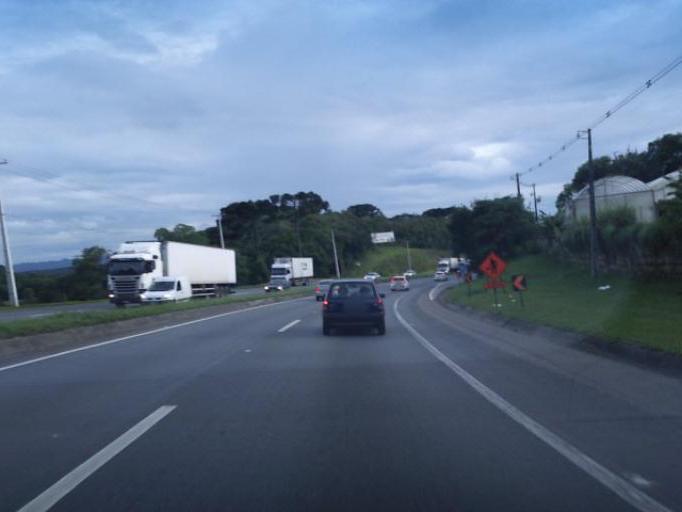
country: BR
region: Parana
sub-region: Sao Jose Dos Pinhais
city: Sao Jose dos Pinhais
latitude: -25.5898
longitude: -49.1716
